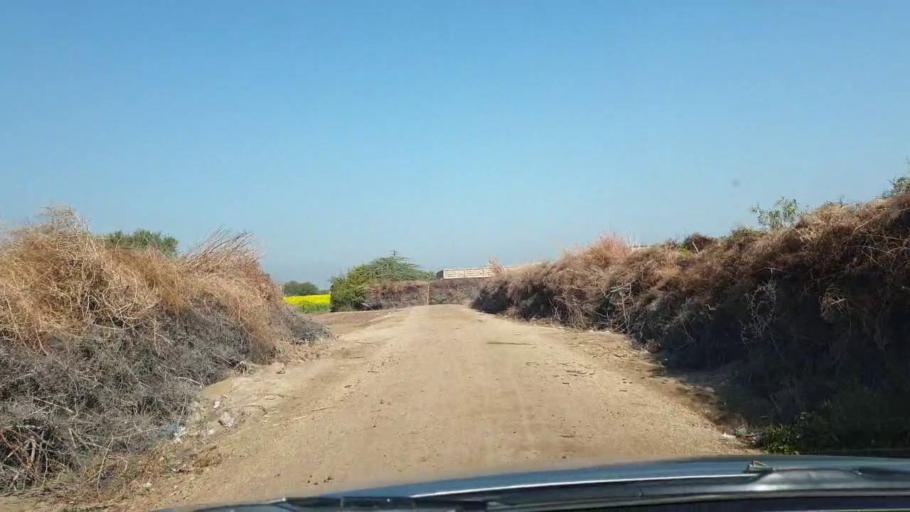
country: PK
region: Sindh
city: Jhol
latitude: 25.8672
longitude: 68.8982
